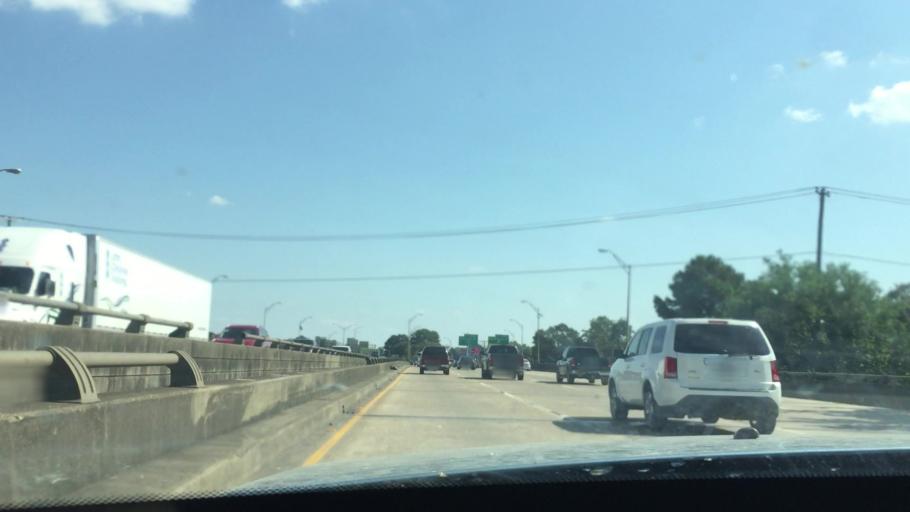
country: US
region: Louisiana
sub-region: East Baton Rouge Parish
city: Baton Rouge
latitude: 30.4348
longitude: -91.1771
